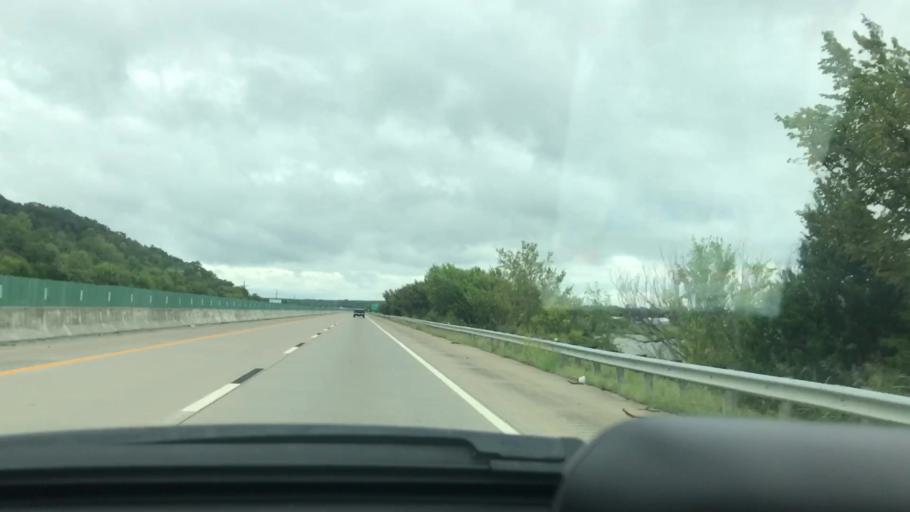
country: US
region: Oklahoma
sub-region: Pittsburg County
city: Krebs
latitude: 35.1195
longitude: -95.6835
